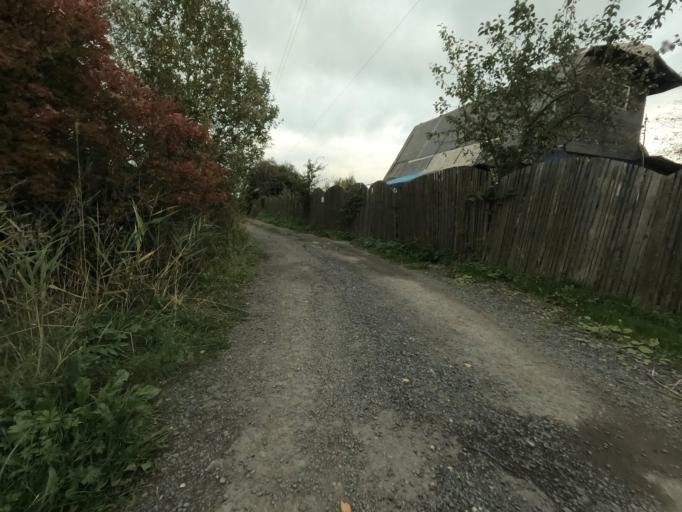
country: RU
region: St.-Petersburg
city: Sapernyy
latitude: 59.7754
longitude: 30.6472
